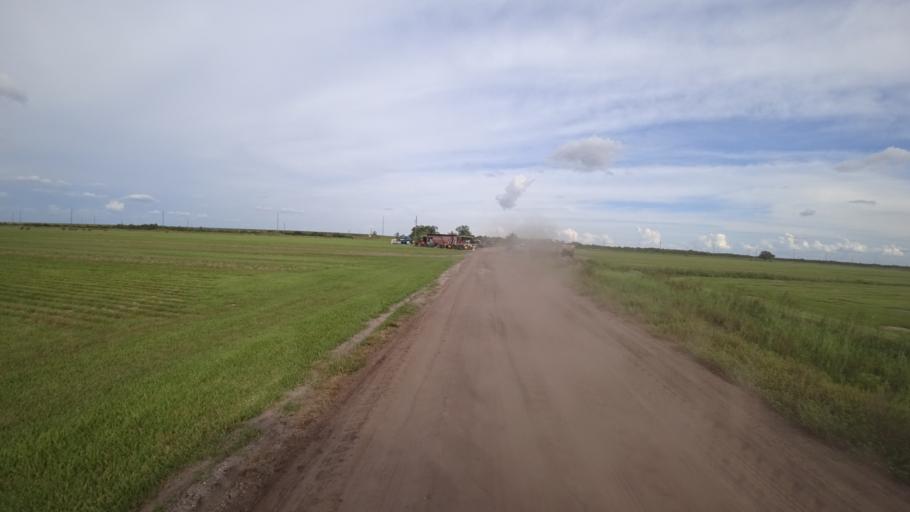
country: US
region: Florida
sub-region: Hardee County
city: Wauchula
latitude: 27.5275
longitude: -82.0791
